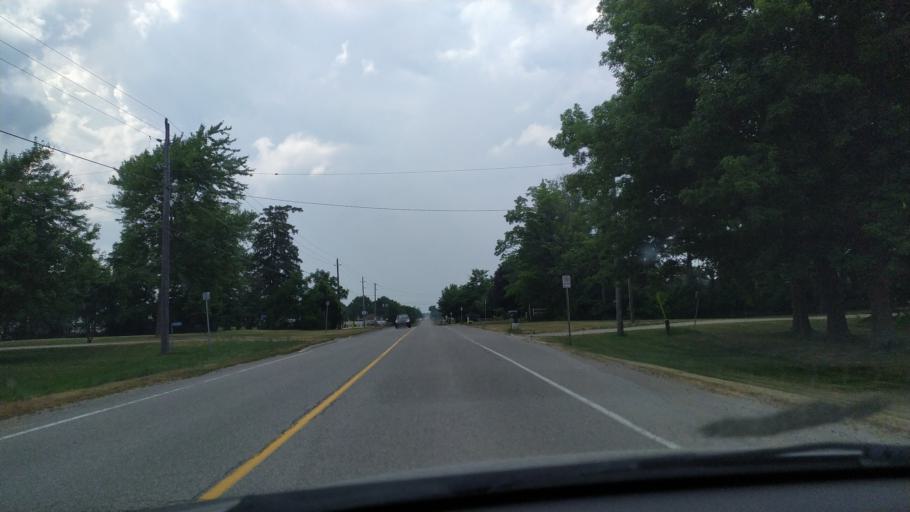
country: CA
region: Ontario
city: Dorchester
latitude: 43.1908
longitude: -81.1477
